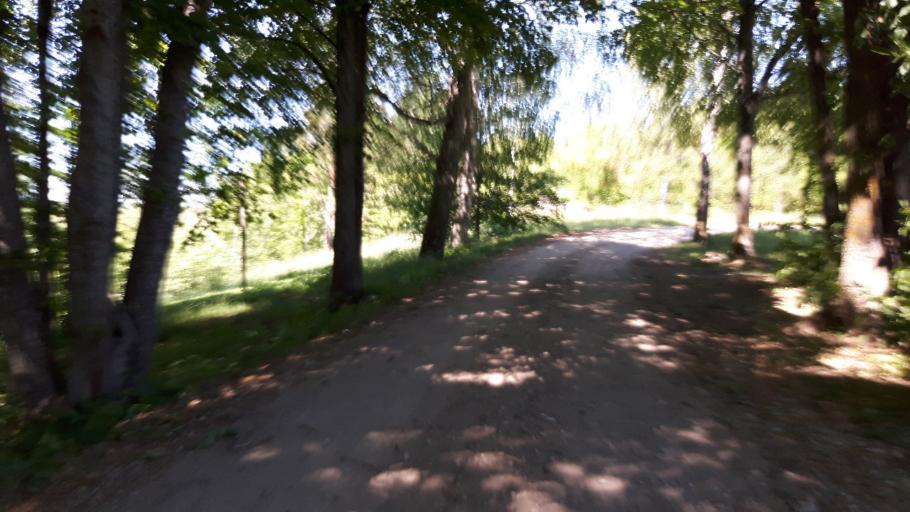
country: LV
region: Kandava
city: Kandava
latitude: 57.0373
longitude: 22.9023
